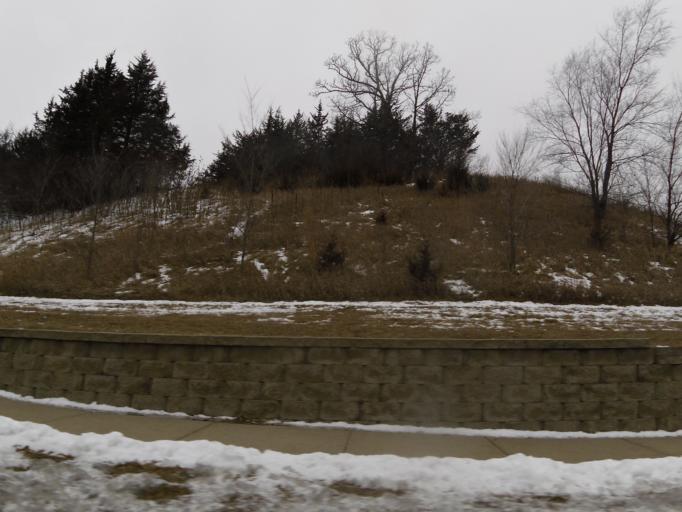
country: US
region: Minnesota
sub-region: Scott County
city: Jordan
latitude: 44.6653
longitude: -93.6337
